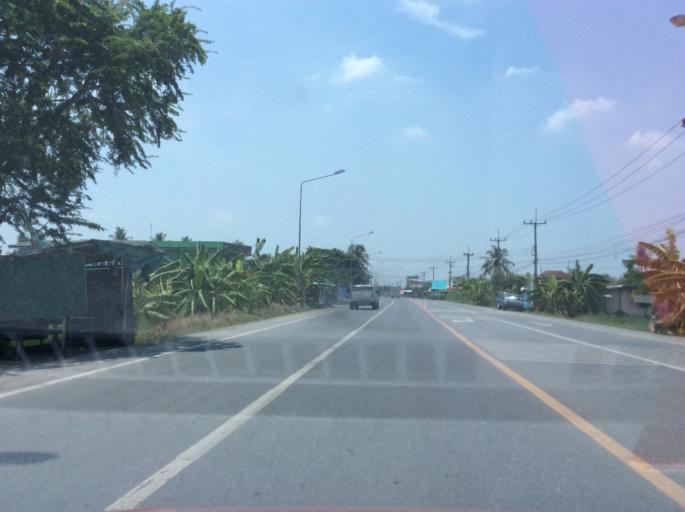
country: TH
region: Pathum Thani
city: Ban Lam Luk Ka
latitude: 13.9861
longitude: 100.7775
